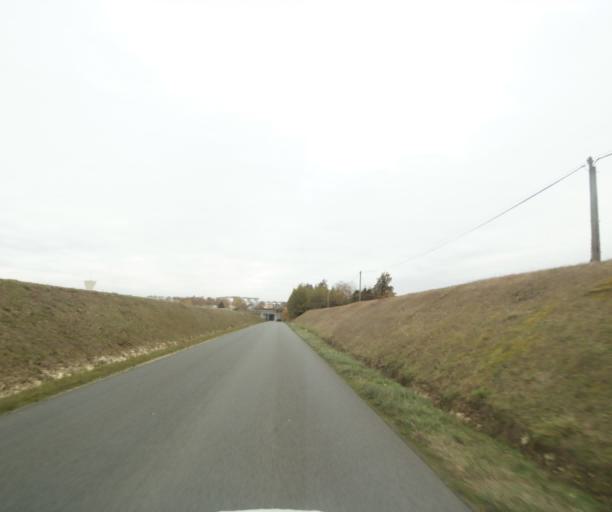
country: FR
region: Poitou-Charentes
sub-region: Departement de la Charente-Maritime
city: Saintes
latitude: 45.7238
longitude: -0.6543
